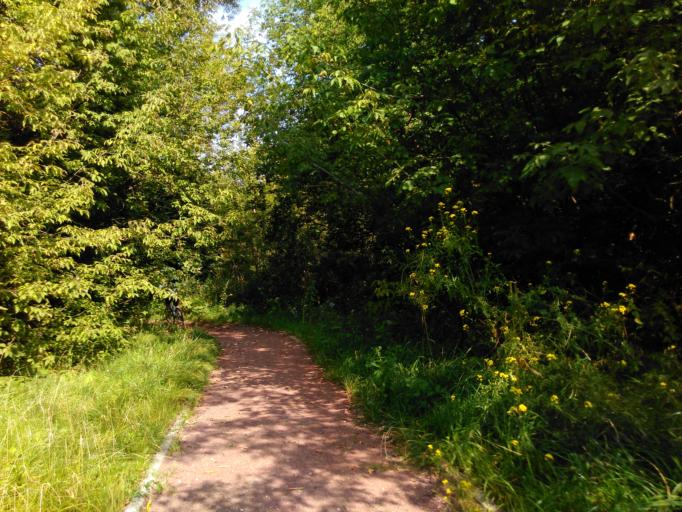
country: RU
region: Moskovskaya
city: Bol'shaya Setun'
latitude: 55.7089
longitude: 37.4144
